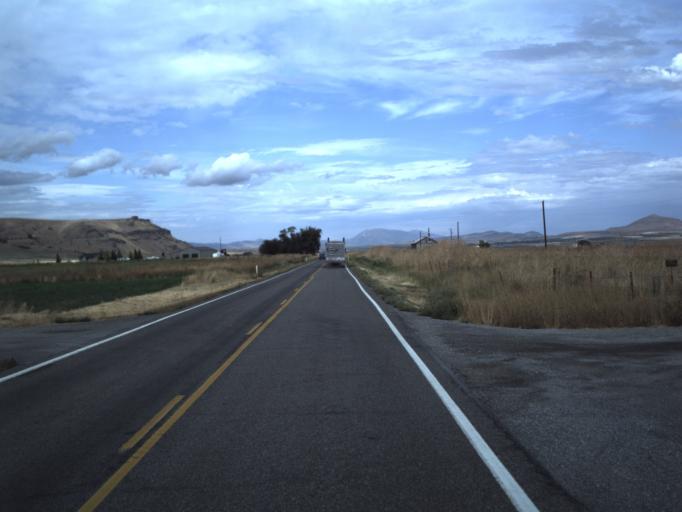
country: US
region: Utah
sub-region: Cache County
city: Mendon
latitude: 41.7645
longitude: -111.9802
